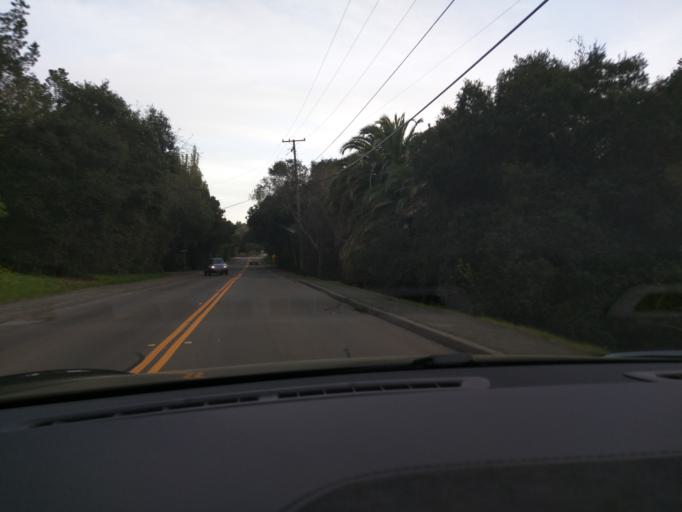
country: US
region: California
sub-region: Santa Clara County
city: Los Altos Hills
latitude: 37.3828
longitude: -122.1512
